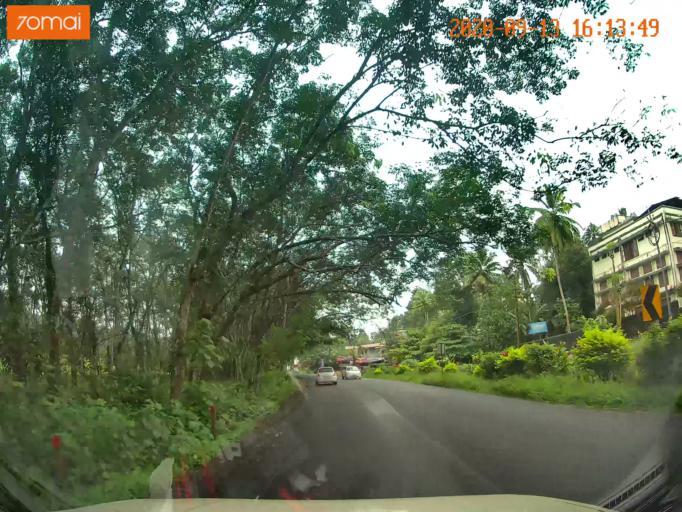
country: IN
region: Kerala
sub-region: Kottayam
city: Palackattumala
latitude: 9.6887
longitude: 76.6296
